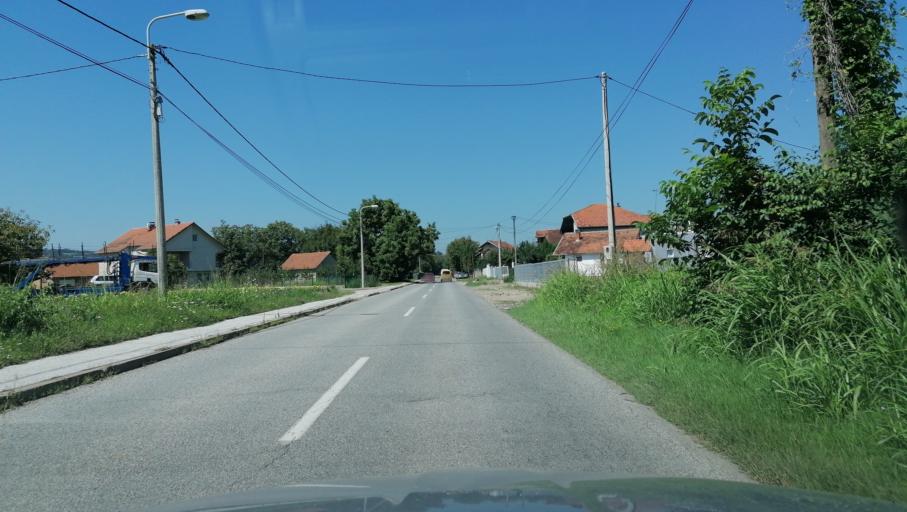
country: RS
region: Central Serbia
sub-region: Raski Okrug
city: Kraljevo
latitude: 43.6908
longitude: 20.6005
